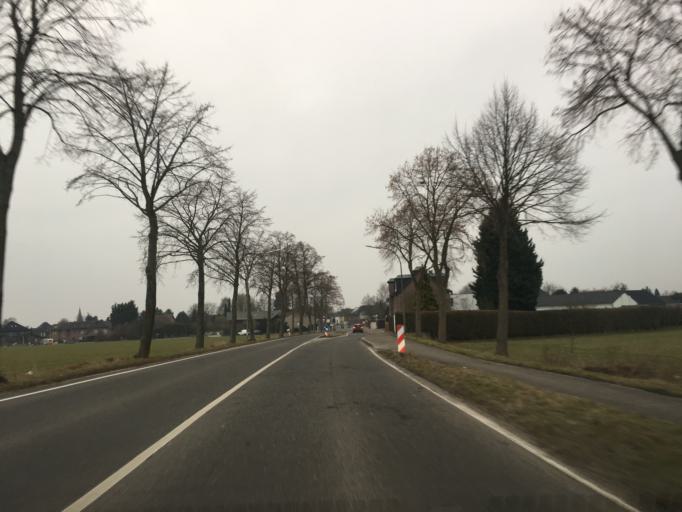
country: DE
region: North Rhine-Westphalia
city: Huckelhoven
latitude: 51.0948
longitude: 6.2275
